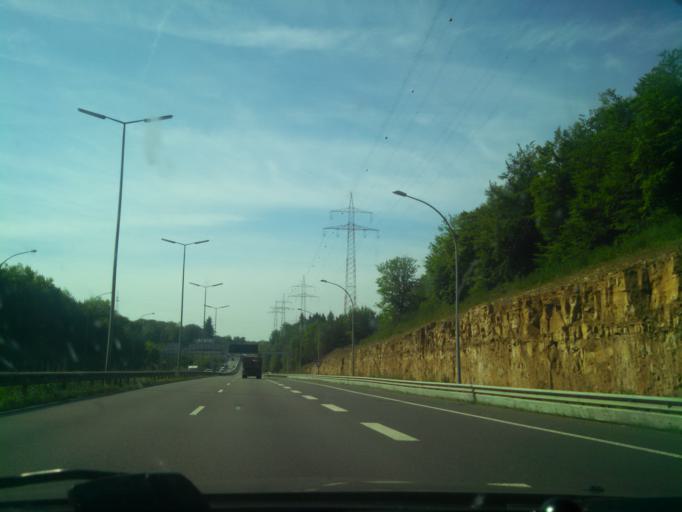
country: LU
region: Luxembourg
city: Kirchberg
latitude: 49.6489
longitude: 6.1864
